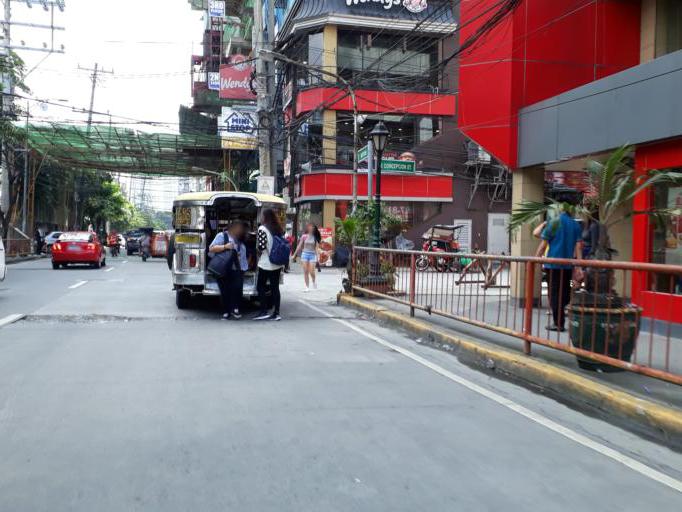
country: PH
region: Metro Manila
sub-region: City of Manila
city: Manila
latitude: 14.6122
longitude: 120.9889
